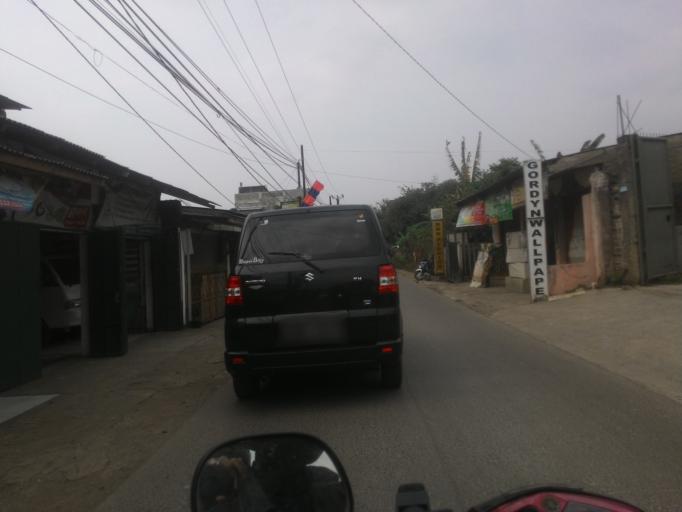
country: ID
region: West Java
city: Depok
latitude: -6.4190
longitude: 106.8411
